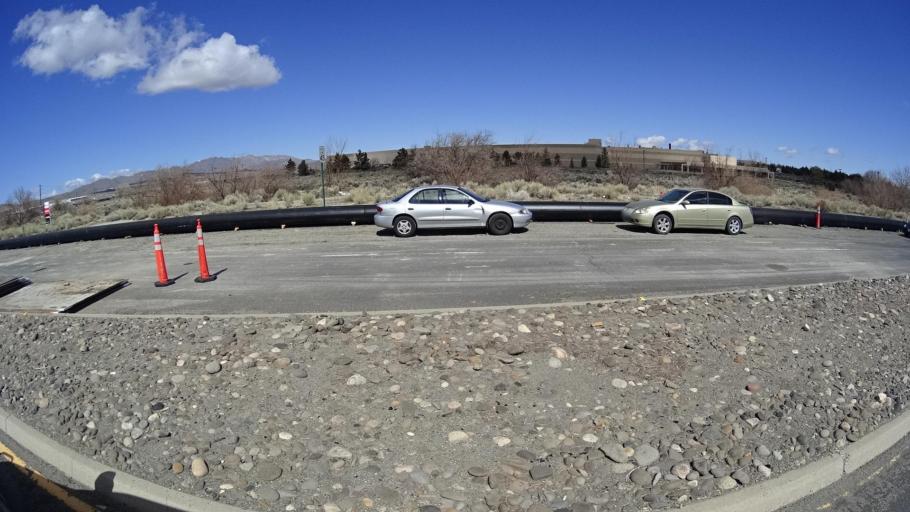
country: US
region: Nevada
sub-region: Washoe County
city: Lemmon Valley
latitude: 39.6425
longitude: -119.8860
